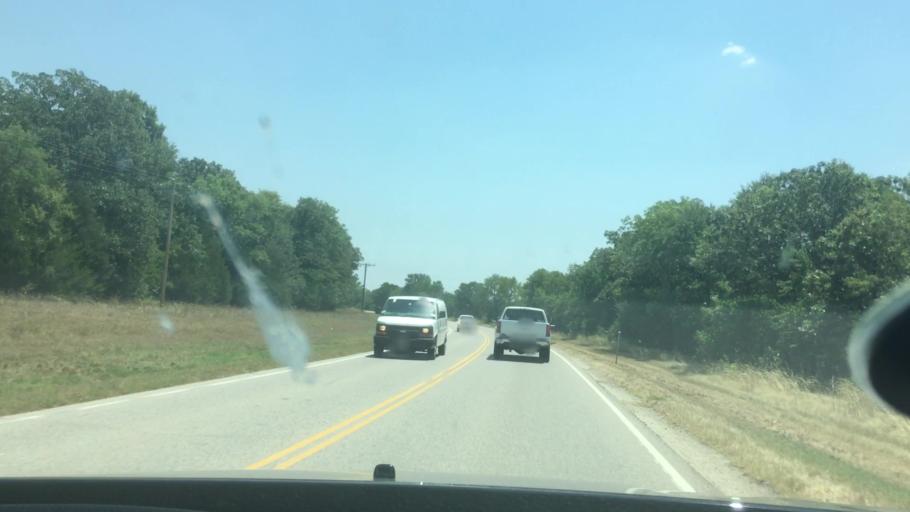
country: US
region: Oklahoma
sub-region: Bryan County
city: Durant
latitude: 34.1774
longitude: -96.4159
